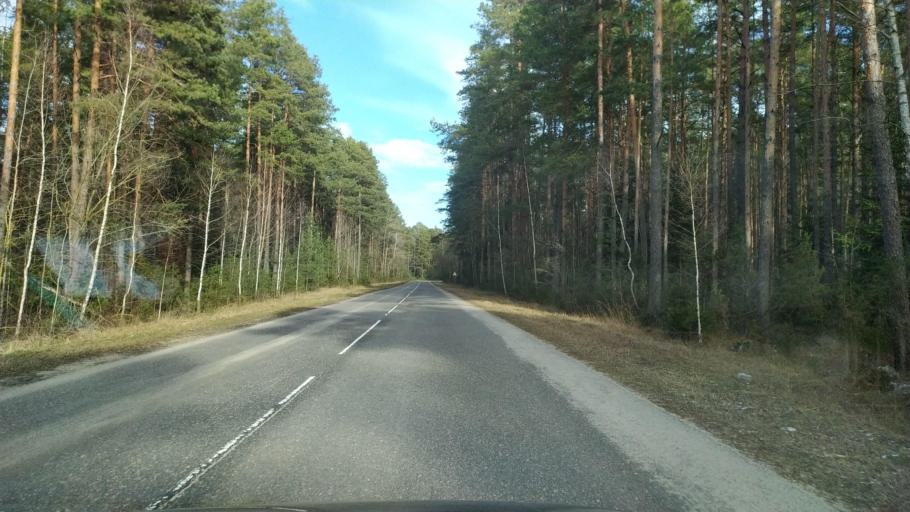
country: BY
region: Brest
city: Pruzhany
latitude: 52.5260
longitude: 24.1766
